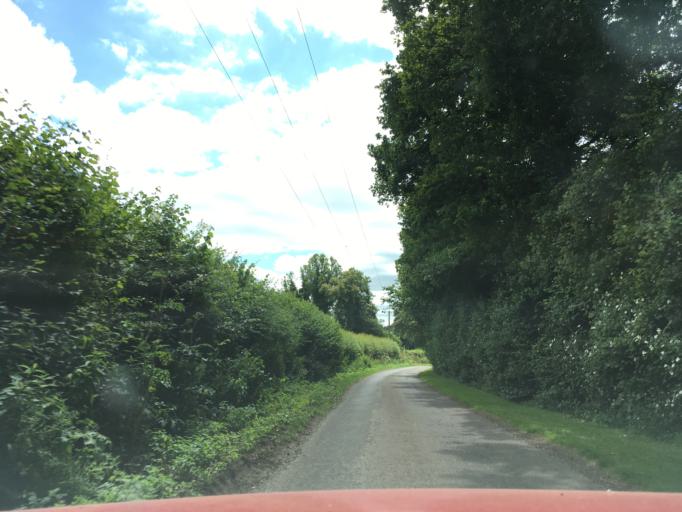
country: GB
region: England
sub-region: Hampshire
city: Highclere
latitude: 51.2859
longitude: -1.4169
